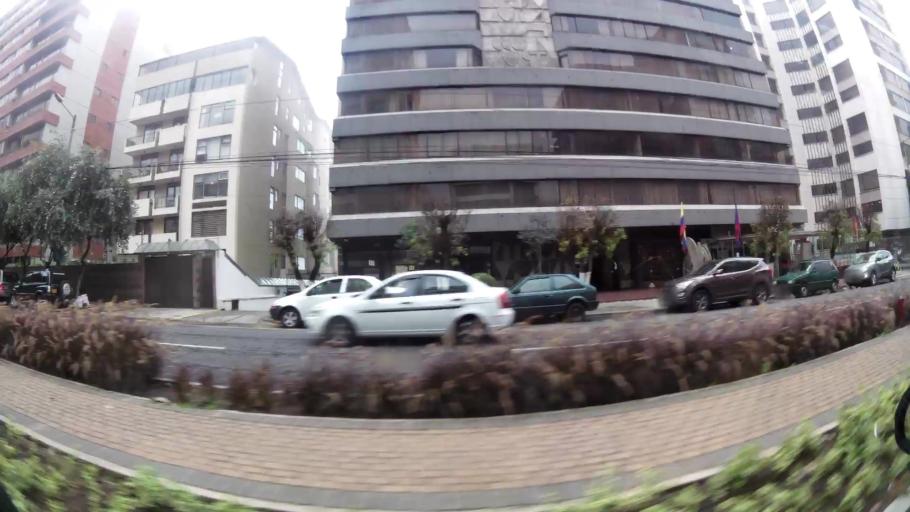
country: EC
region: Pichincha
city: Quito
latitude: -0.1963
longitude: -78.4785
